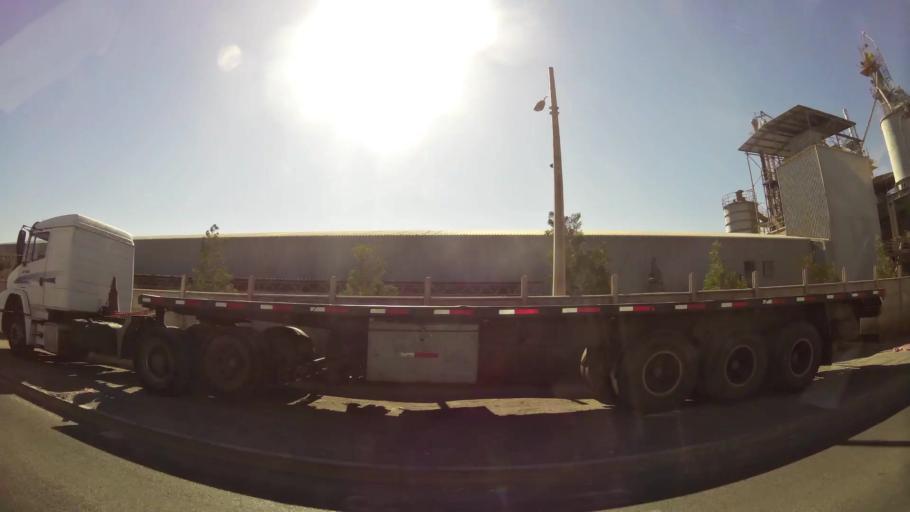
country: CL
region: Santiago Metropolitan
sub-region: Provincia de Maipo
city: San Bernardo
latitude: -33.5572
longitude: -70.6958
